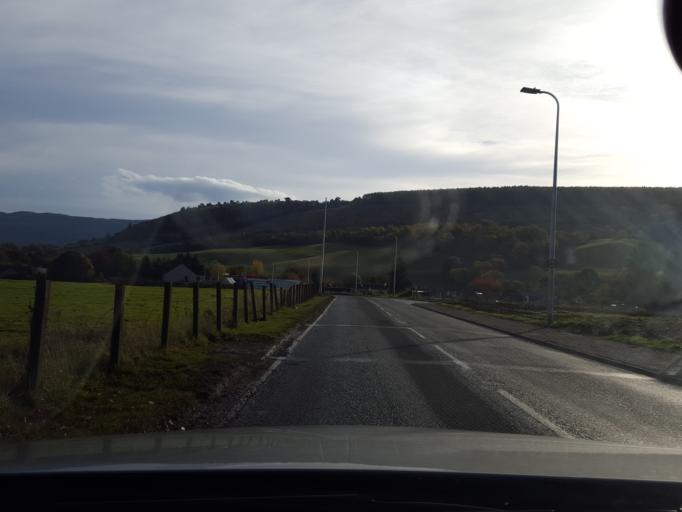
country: GB
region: Scotland
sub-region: Highland
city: Beauly
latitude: 57.3292
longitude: -4.4786
